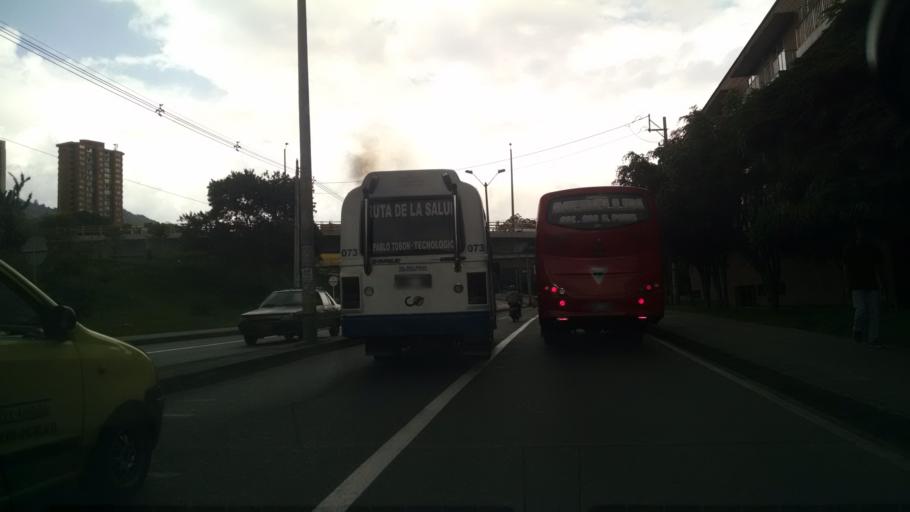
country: CO
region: Antioquia
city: Medellin
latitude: 6.2711
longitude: -75.5947
